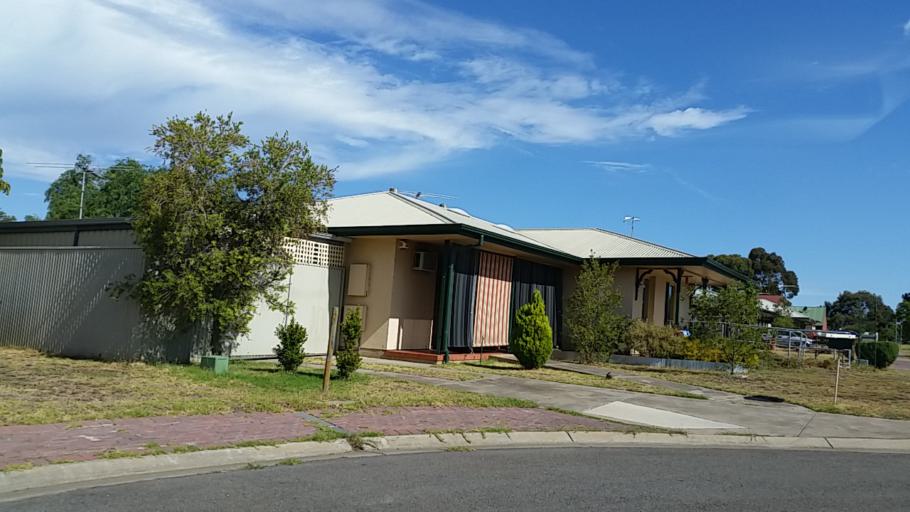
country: AU
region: South Australia
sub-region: Port Adelaide Enfield
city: Alberton
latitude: -34.8532
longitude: 138.5355
